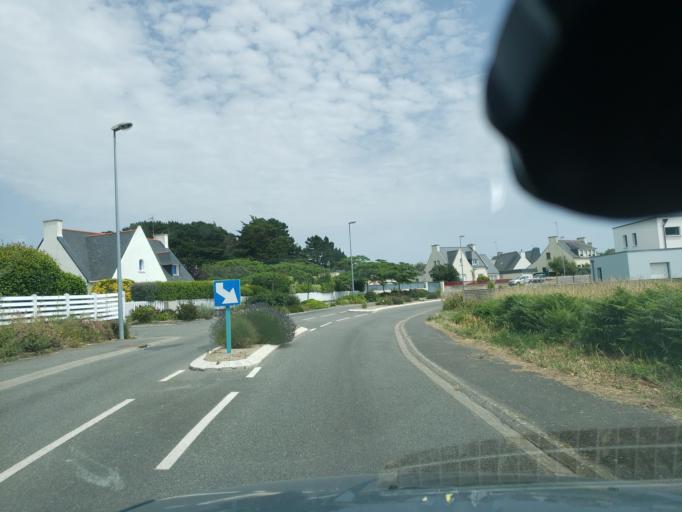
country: FR
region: Brittany
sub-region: Departement du Finistere
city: Guilvinec
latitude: 47.8018
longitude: -4.2682
